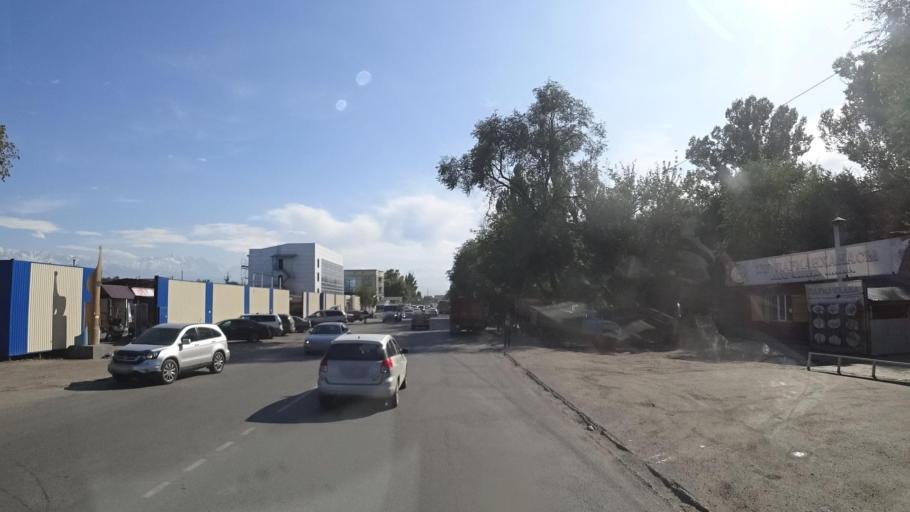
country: KZ
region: Almaty Oblysy
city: Energeticheskiy
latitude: 43.4188
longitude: 77.0219
